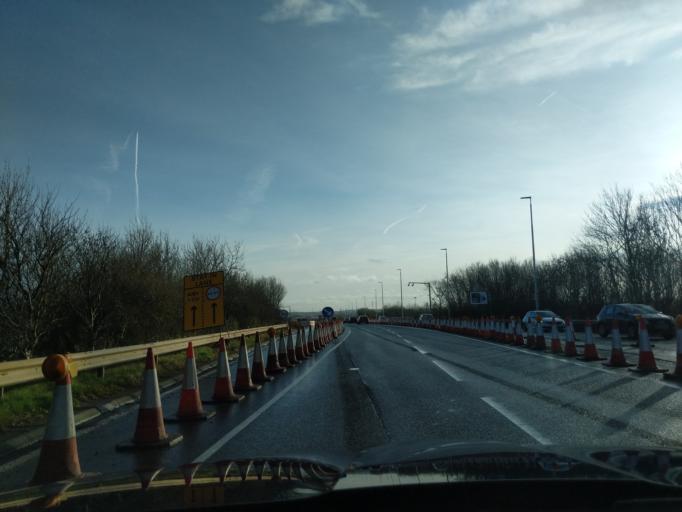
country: GB
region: England
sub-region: Borough of North Tyneside
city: Shiremoor
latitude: 55.0137
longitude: -1.5047
